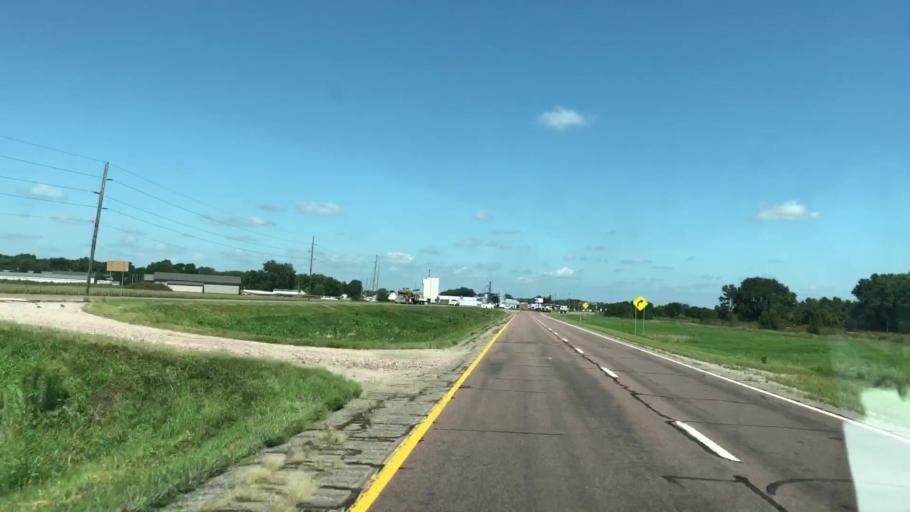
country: US
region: Iowa
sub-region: Plymouth County
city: Le Mars
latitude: 42.7103
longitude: -96.2523
